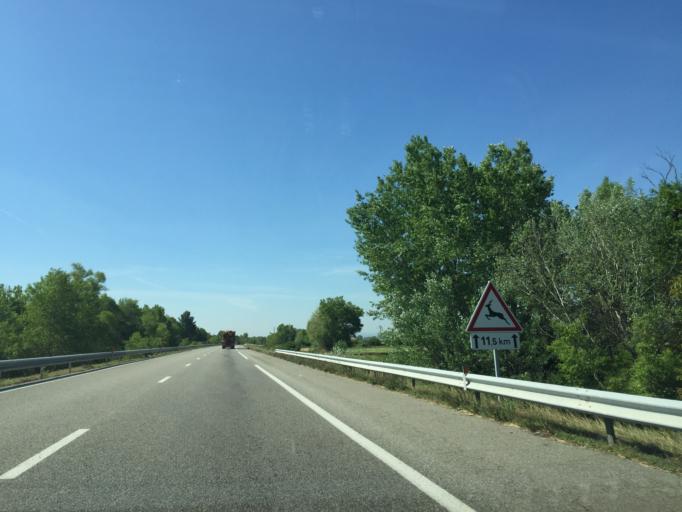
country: FR
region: Provence-Alpes-Cote d'Azur
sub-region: Departement des Alpes-de-Haute-Provence
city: Villeneuve
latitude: 43.8871
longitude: 5.8804
